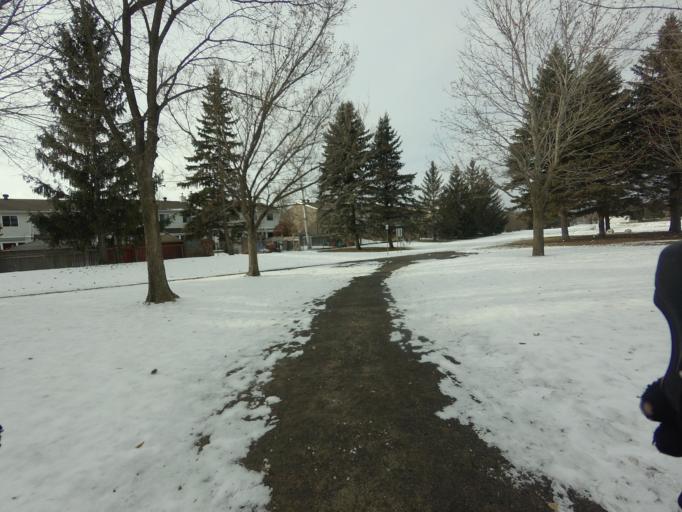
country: CA
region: Ontario
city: Bells Corners
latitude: 45.2688
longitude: -75.7688
